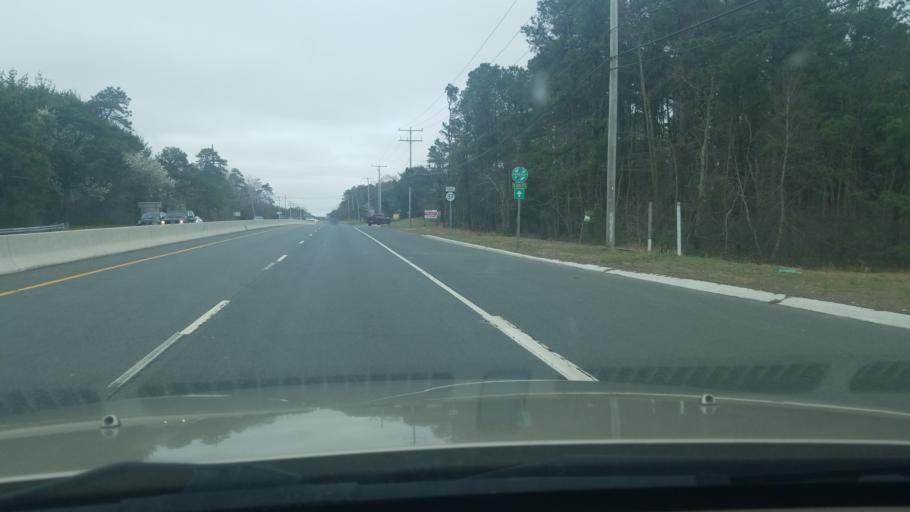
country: US
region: New Jersey
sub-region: Ocean County
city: Leisure Knoll
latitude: 40.0012
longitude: -74.2894
